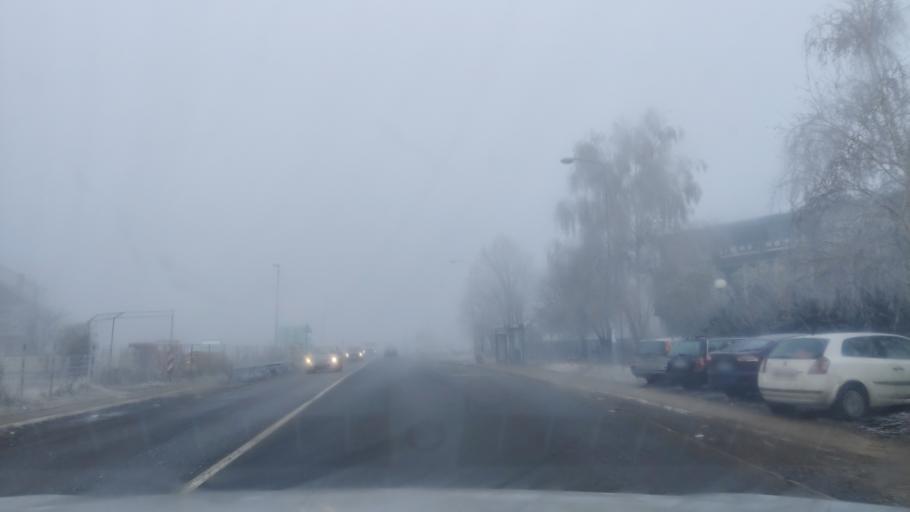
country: RS
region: Central Serbia
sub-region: Belgrade
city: Stari Grad
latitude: 44.8834
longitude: 20.4636
